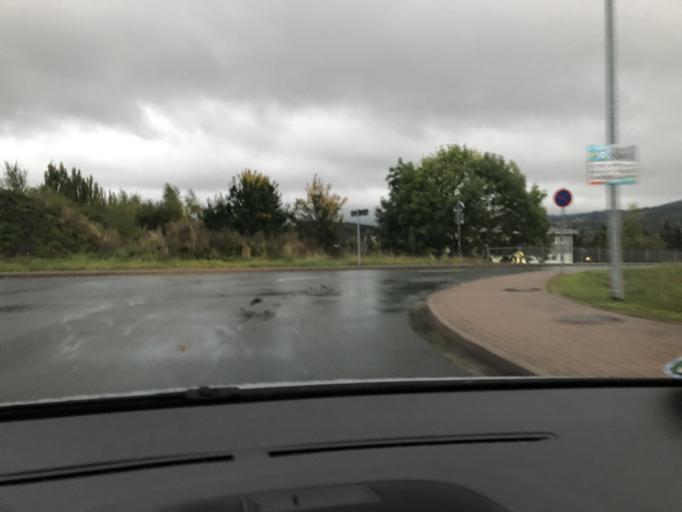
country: DE
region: Thuringia
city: Neuhaus
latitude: 50.6929
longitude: 10.9371
